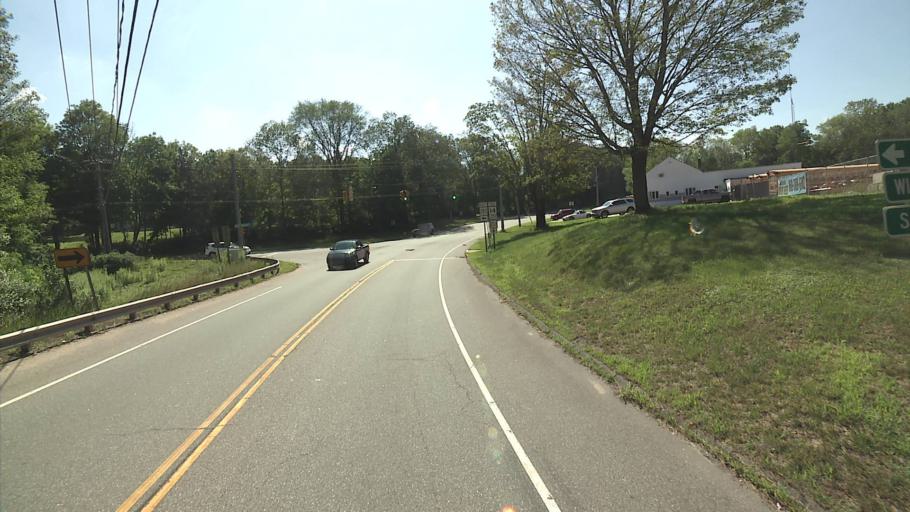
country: US
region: Connecticut
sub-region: Windham County
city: Windham
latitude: 41.7100
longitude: -72.1664
